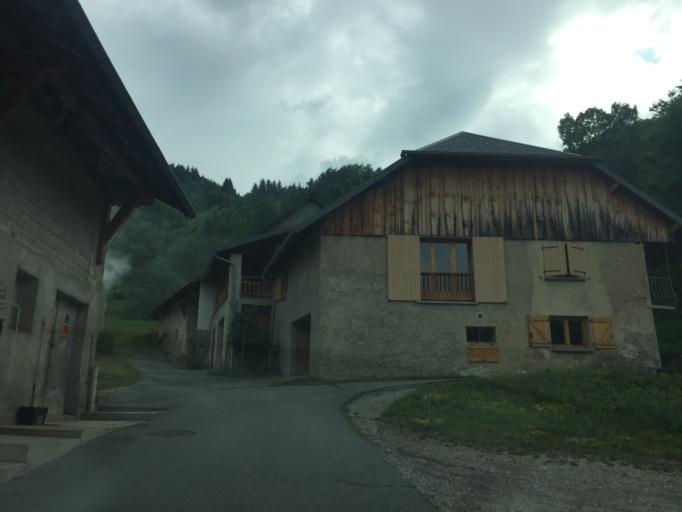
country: FR
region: Rhone-Alpes
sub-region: Departement de la Savoie
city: Montmelian
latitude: 45.5284
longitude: 6.0616
